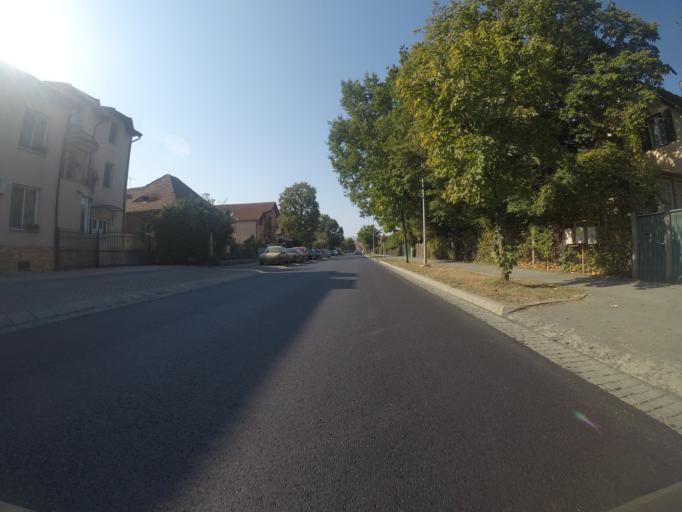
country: RO
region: Sibiu
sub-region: Municipiul Sibiu
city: Sibiu
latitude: 45.7883
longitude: 24.1635
